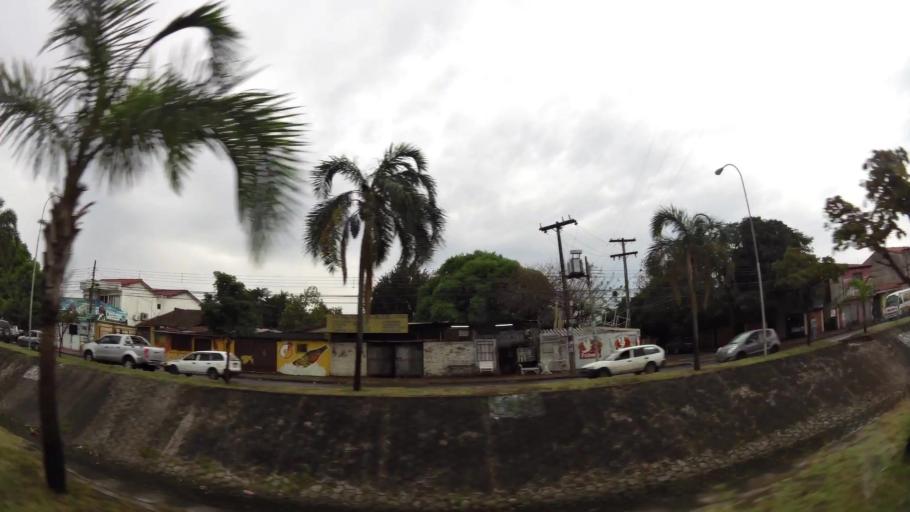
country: BO
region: Santa Cruz
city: Santa Cruz de la Sierra
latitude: -17.7814
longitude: -63.1572
